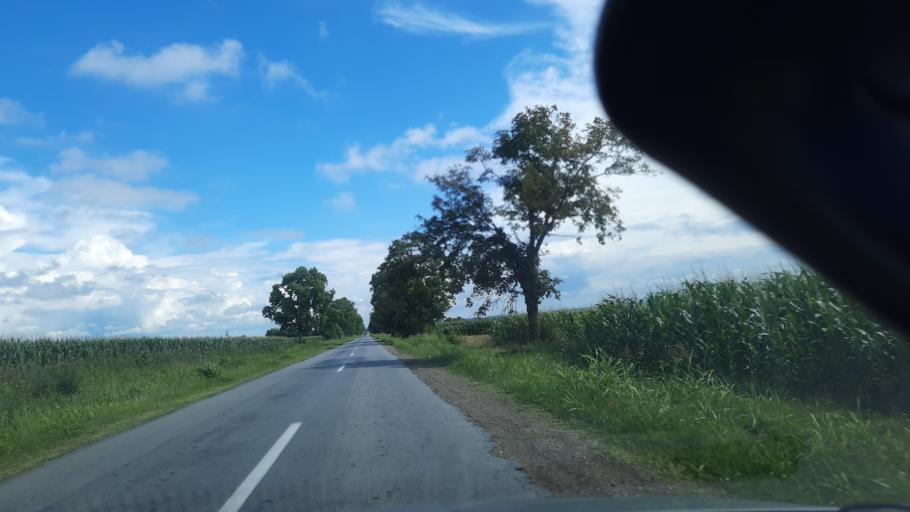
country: RS
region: Autonomna Pokrajina Vojvodina
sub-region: Sremski Okrug
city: Sremska Mitrovica
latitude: 45.0751
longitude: 19.5896
